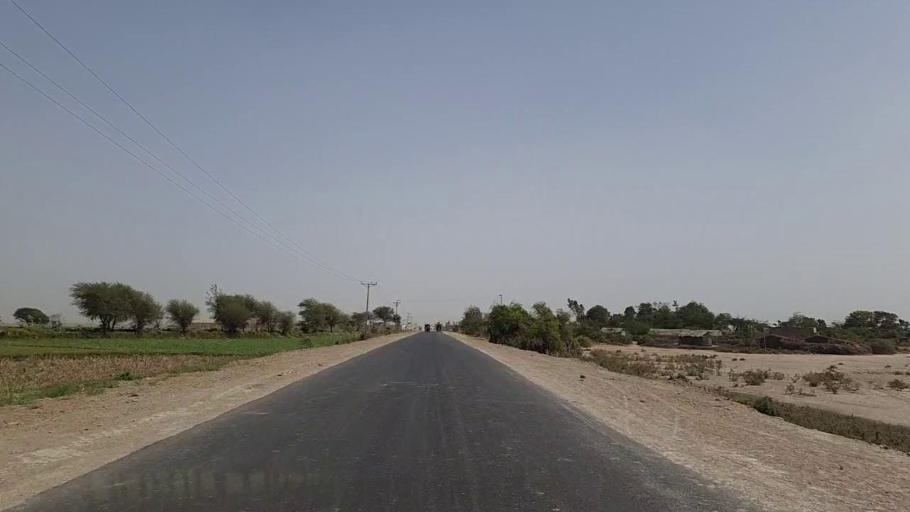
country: PK
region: Sindh
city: Tando Bago
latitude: 24.8006
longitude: 68.9426
